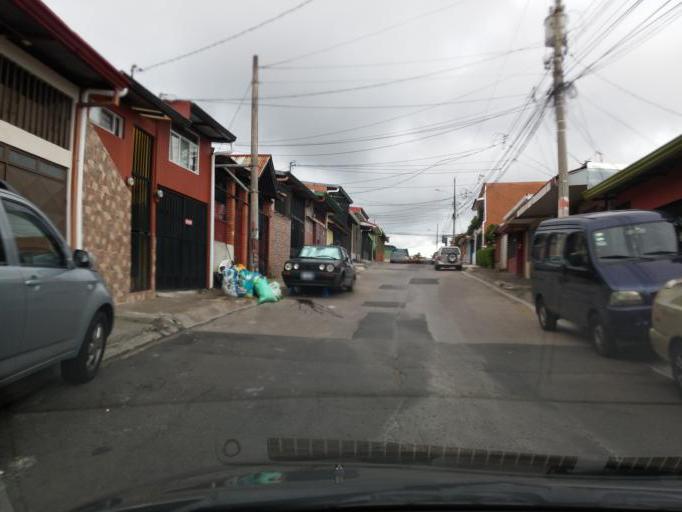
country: CR
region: Heredia
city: Mercedes
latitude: 10.0221
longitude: -84.1296
